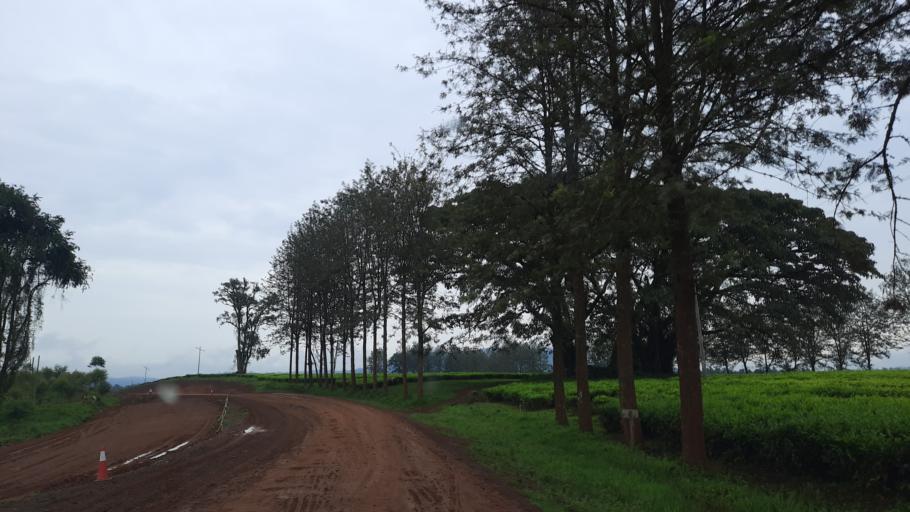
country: ET
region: Oromiya
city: Gore
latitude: 7.8437
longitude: 35.4767
